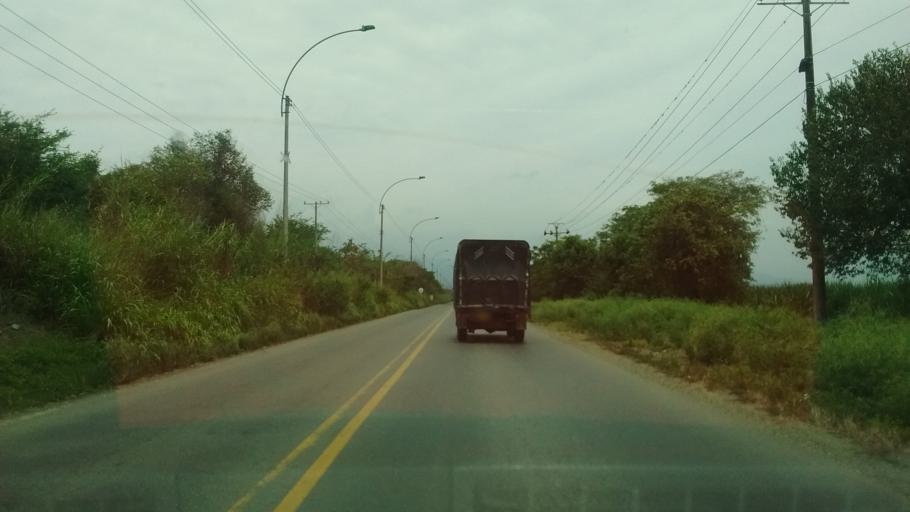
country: CO
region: Valle del Cauca
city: Jamundi
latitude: 3.3235
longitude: -76.4996
